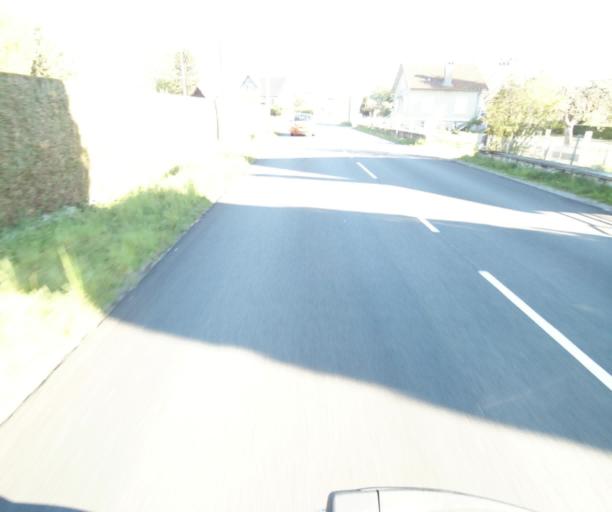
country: FR
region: Limousin
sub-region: Departement de la Correze
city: Correze
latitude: 45.3398
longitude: 1.8749
